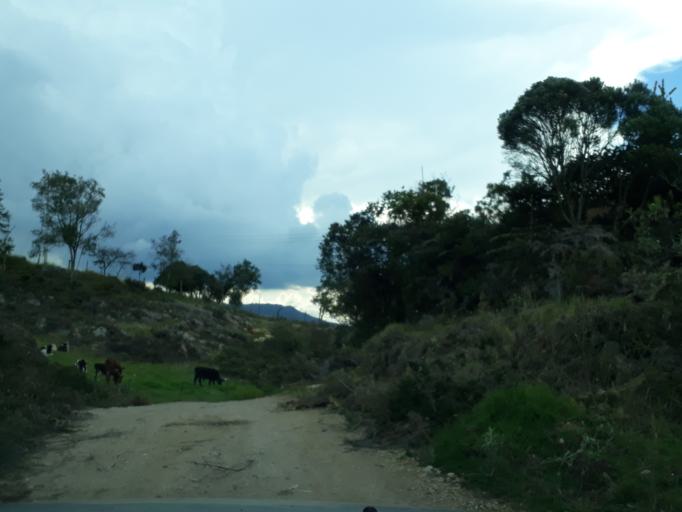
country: CO
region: Cundinamarca
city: Lenguazaque
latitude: 5.2561
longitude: -73.6861
